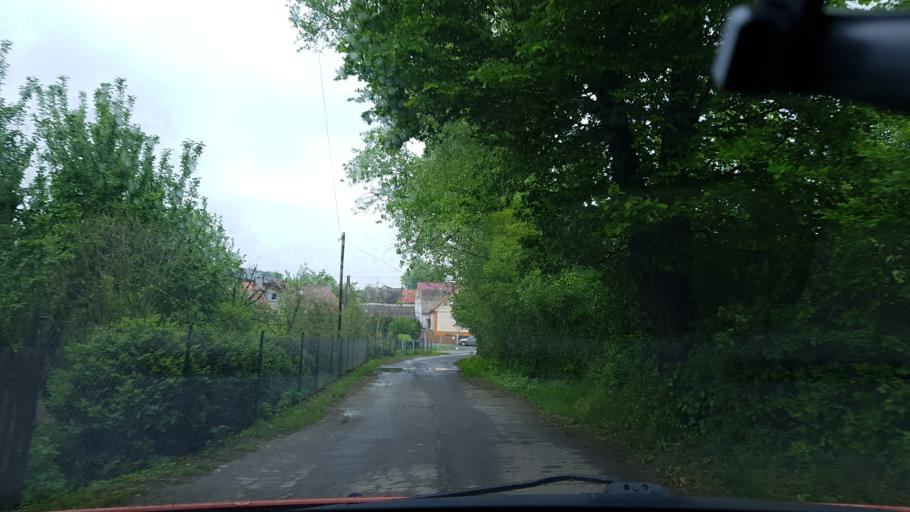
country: PL
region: Lower Silesian Voivodeship
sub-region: Powiat zabkowicki
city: Bardo
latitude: 50.5527
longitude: 16.7557
